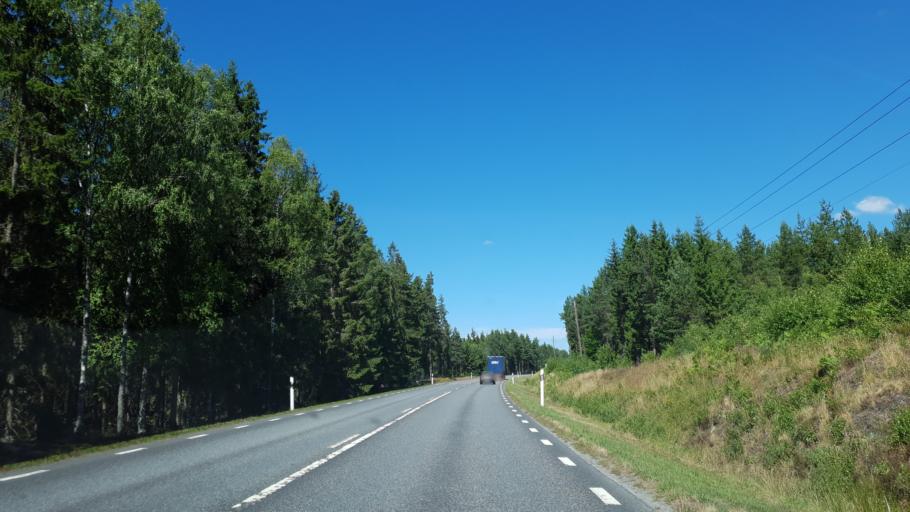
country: SE
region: Joenkoeping
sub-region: Varnamo Kommun
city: Rydaholm
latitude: 57.0451
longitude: 14.2302
